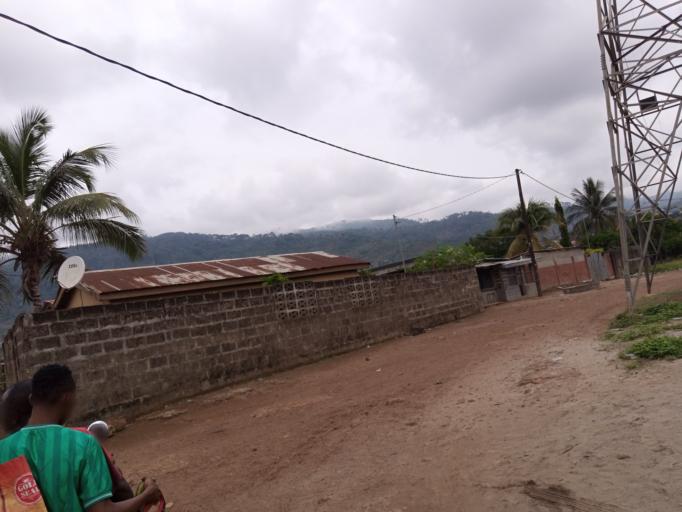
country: SL
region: Western Area
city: Hastings
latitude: 8.3823
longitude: -13.1489
